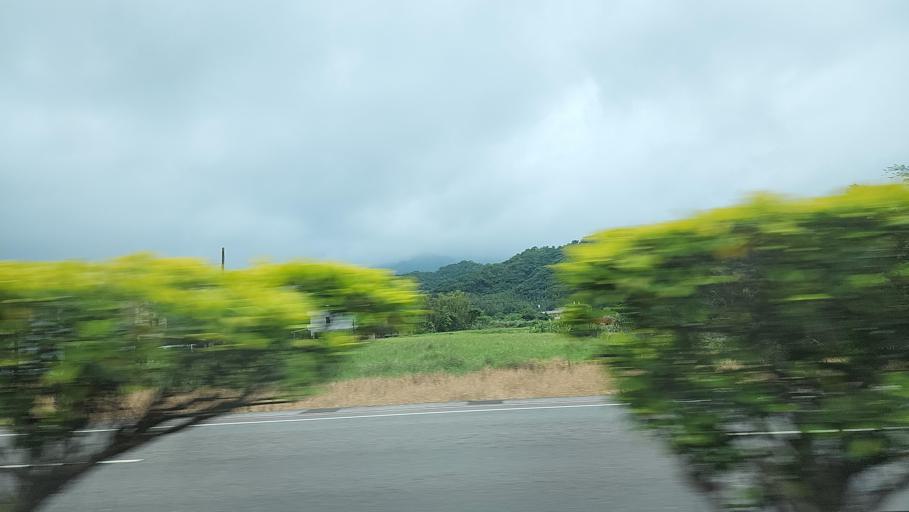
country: TW
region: Taiwan
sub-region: Keelung
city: Keelung
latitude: 25.2104
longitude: 121.6491
